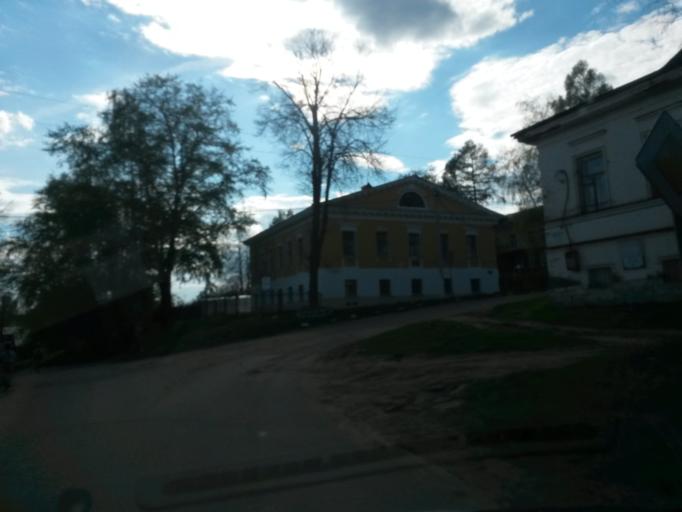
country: RU
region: Jaroslavl
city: Myshkin
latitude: 57.7833
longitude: 38.4502
